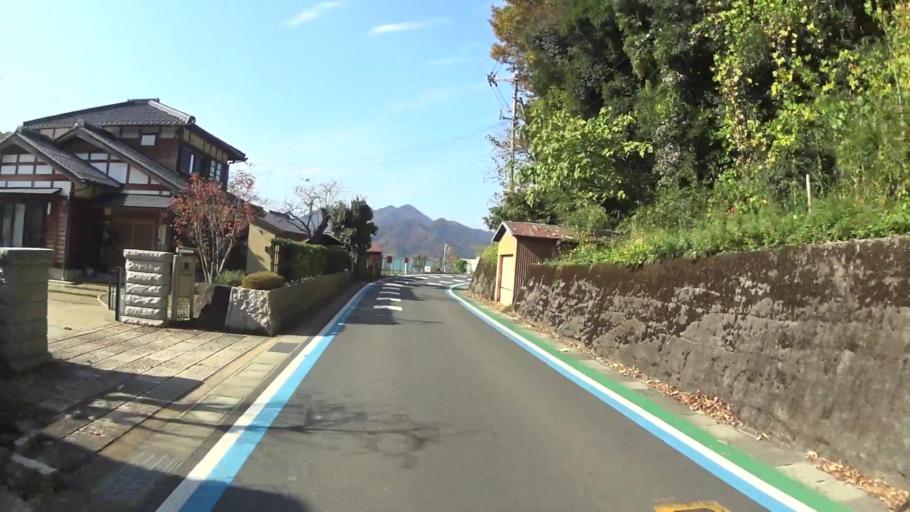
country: JP
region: Kyoto
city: Maizuru
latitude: 35.4777
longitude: 135.3472
